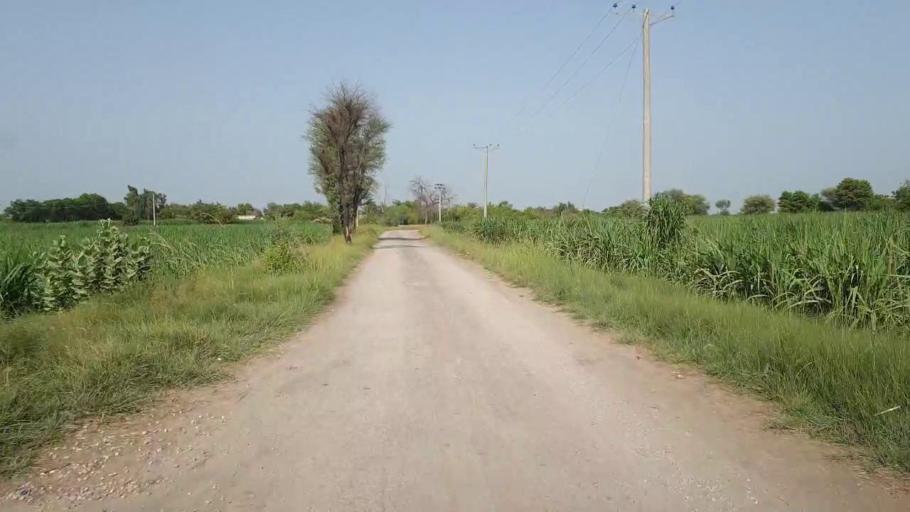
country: PK
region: Sindh
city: Daur
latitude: 26.3227
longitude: 68.1514
